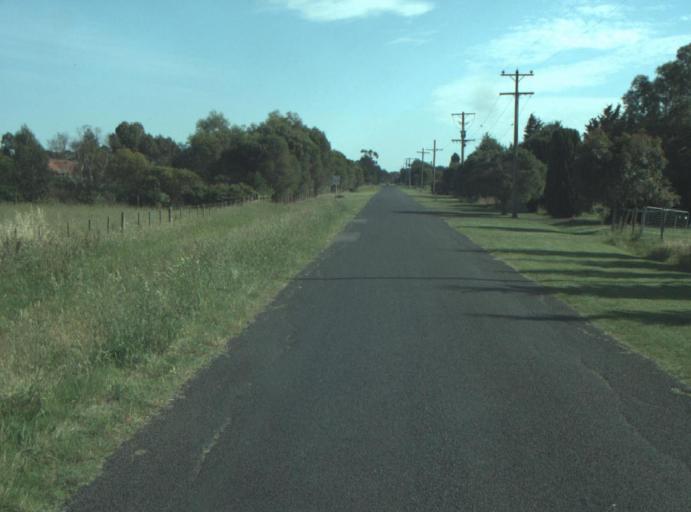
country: AU
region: Victoria
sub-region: Greater Geelong
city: Leopold
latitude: -38.1808
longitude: 144.4380
